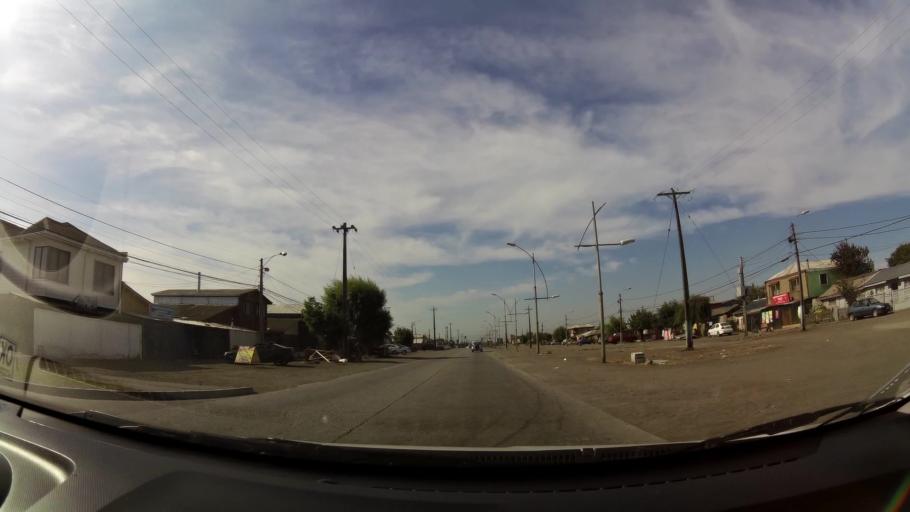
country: CL
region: Biobio
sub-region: Provincia de Concepcion
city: Talcahuano
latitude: -36.7832
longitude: -73.1111
